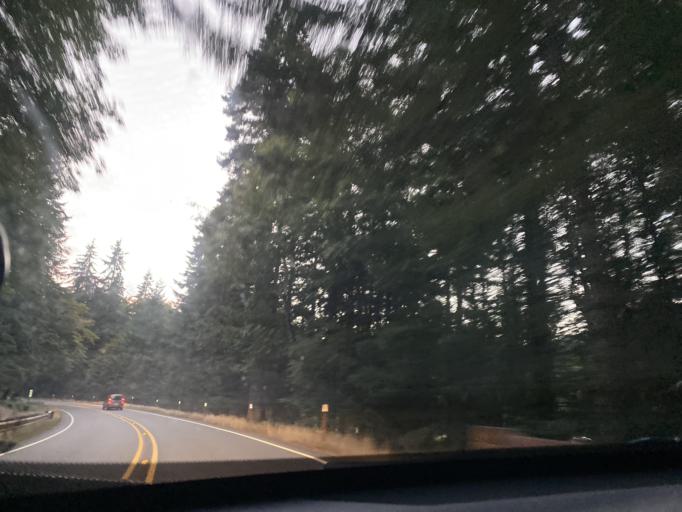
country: CA
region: British Columbia
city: Sooke
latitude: 48.0579
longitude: -123.7865
